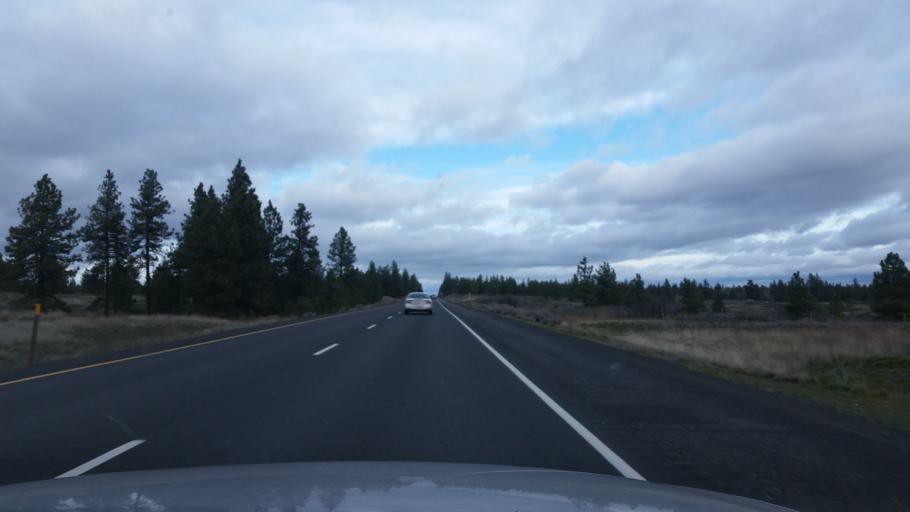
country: US
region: Washington
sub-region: Spokane County
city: Medical Lake
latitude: 47.4159
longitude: -117.8150
